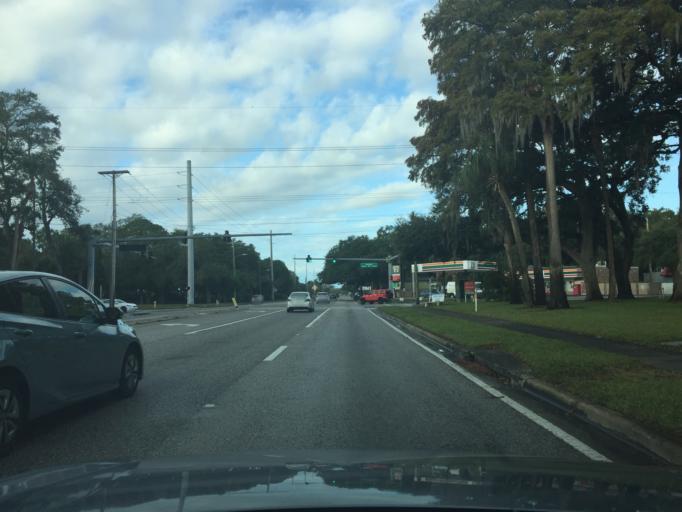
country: US
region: Florida
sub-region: Hillsborough County
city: Town 'n' Country
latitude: 27.9819
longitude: -82.5498
